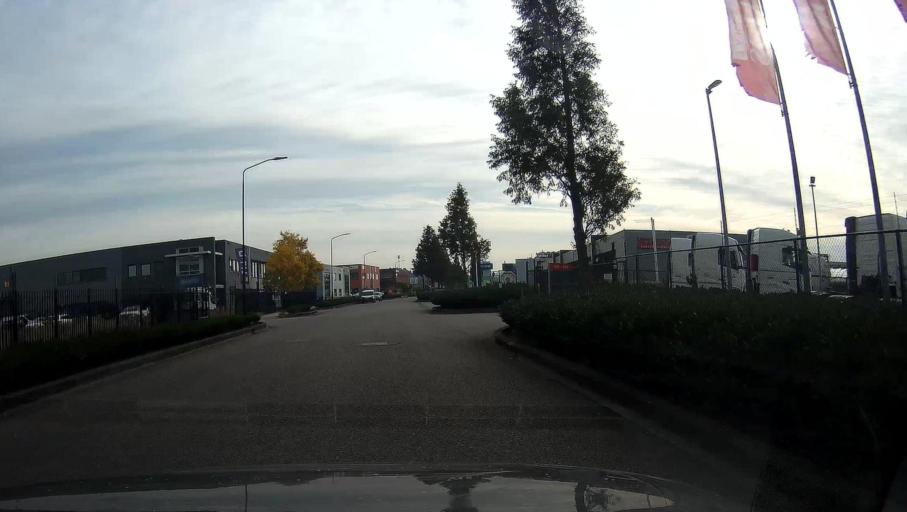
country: NL
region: South Holland
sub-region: Gemeente Papendrecht
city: Papendrecht
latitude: 51.8447
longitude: 4.6755
